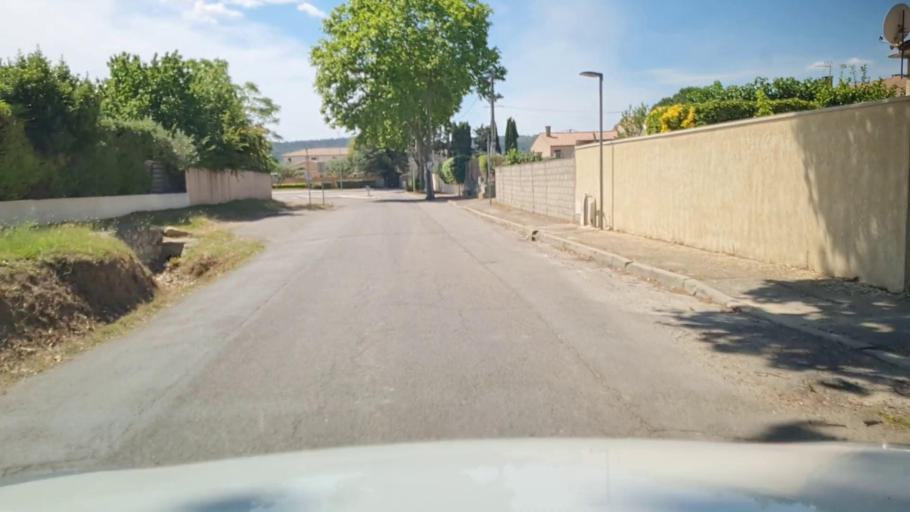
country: FR
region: Languedoc-Roussillon
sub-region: Departement du Gard
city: Clarensac
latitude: 43.8248
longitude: 4.2251
